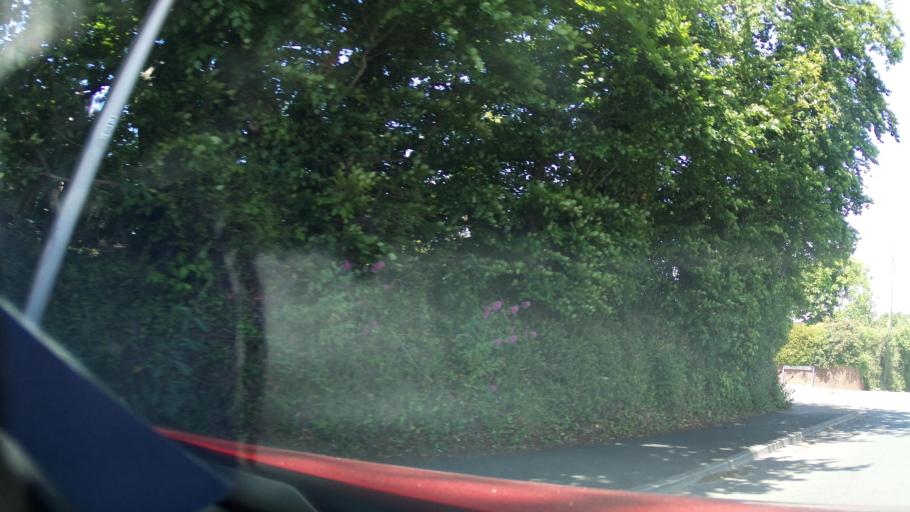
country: GB
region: England
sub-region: Devon
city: Exmouth
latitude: 50.6358
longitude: -3.4106
